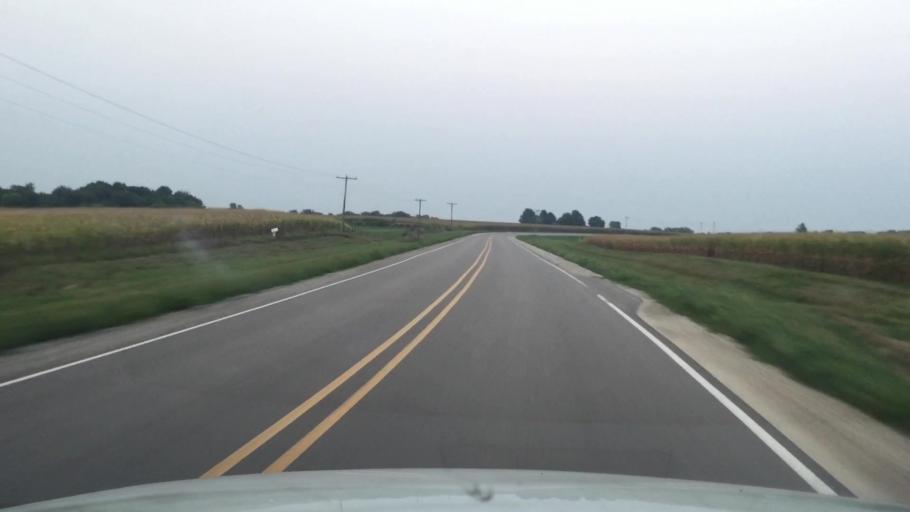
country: US
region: Iowa
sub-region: Warren County
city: Indianola
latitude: 41.1829
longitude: -93.4495
